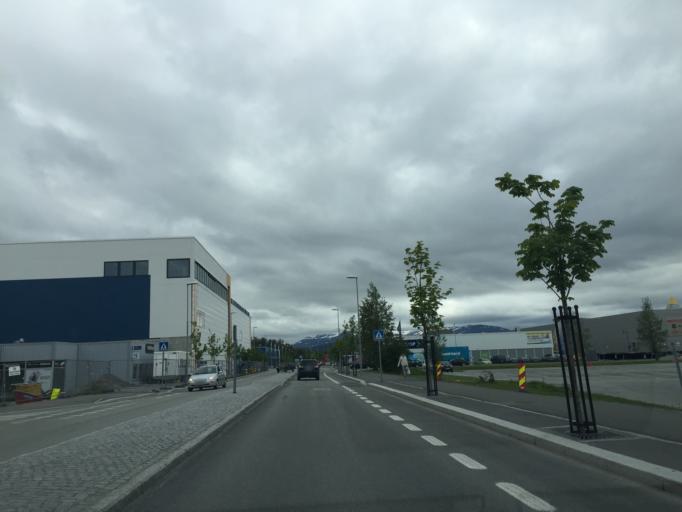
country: NO
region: Nordland
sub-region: Bodo
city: Bodo
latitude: 67.2785
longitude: 14.4179
